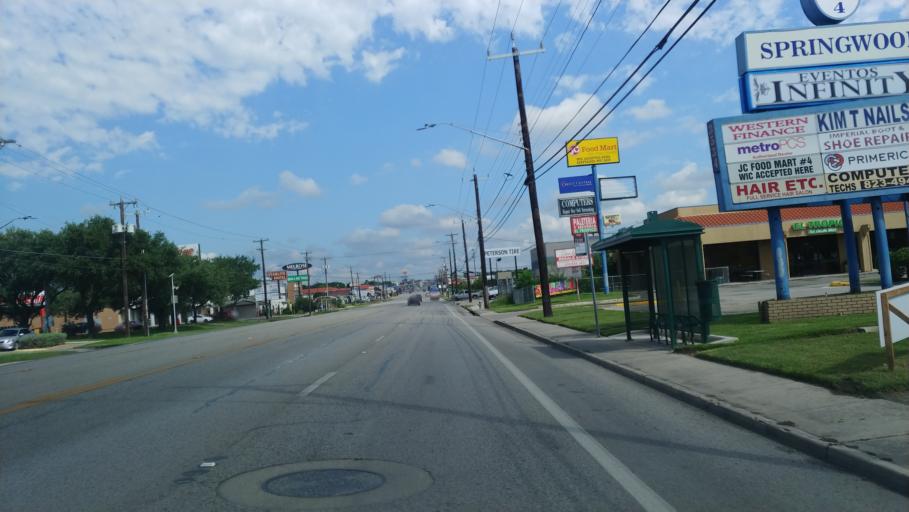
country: US
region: Texas
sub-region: Bexar County
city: Balcones Heights
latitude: 29.4772
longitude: -98.5385
